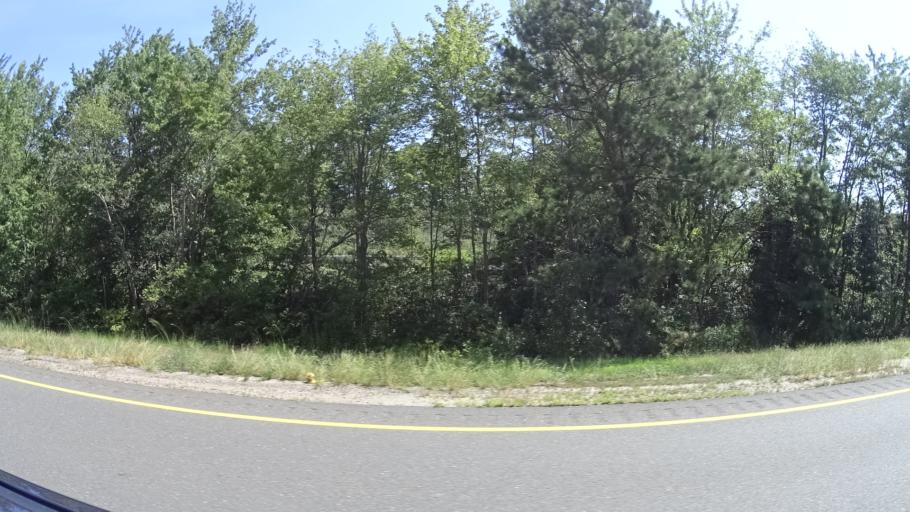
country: US
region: New Jersey
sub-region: Monmouth County
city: Wanamassa
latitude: 40.2334
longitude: -74.0508
